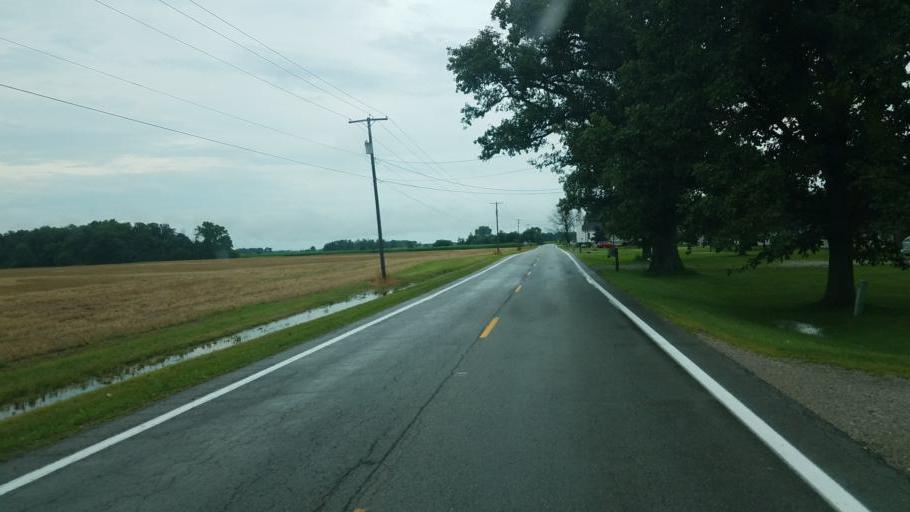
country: US
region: Ohio
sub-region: Marion County
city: Prospect
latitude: 40.5176
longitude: -83.2399
